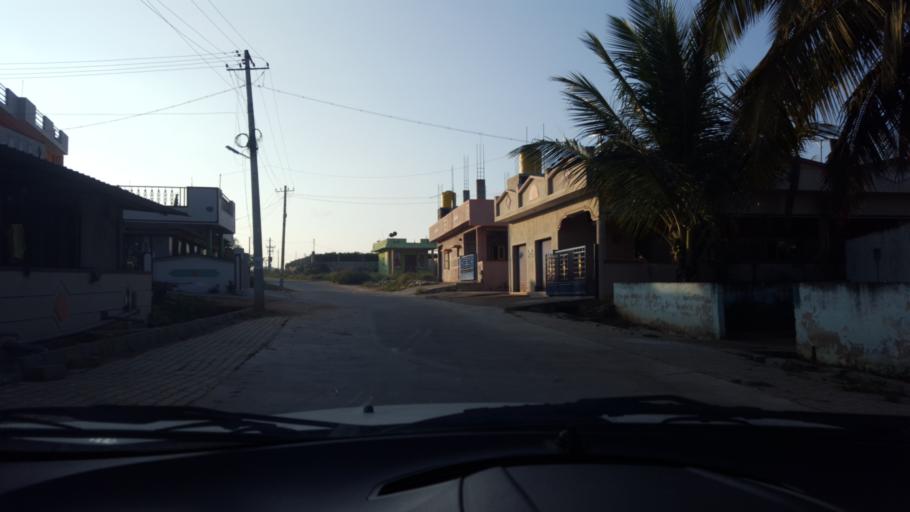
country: IN
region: Karnataka
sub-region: Bangalore Urban
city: Yelahanka
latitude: 13.1877
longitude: 77.6081
